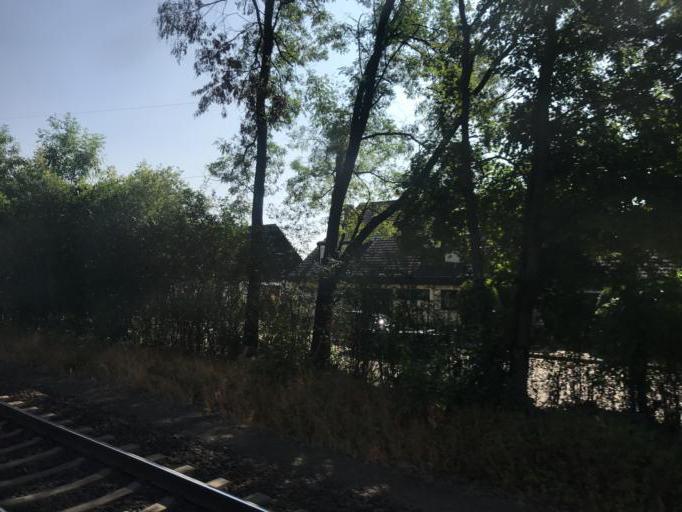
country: DE
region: Saarland
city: Sulzbach
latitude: 49.3064
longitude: 7.0743
